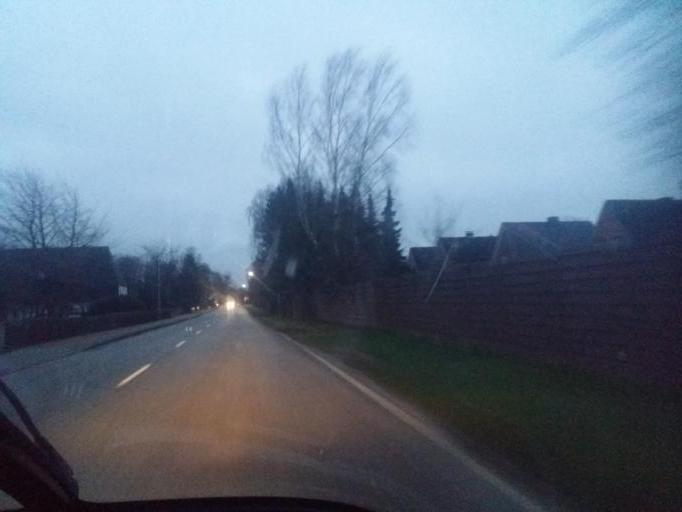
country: DE
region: Schleswig-Holstein
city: Schenefeld
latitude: 54.0529
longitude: 9.4793
